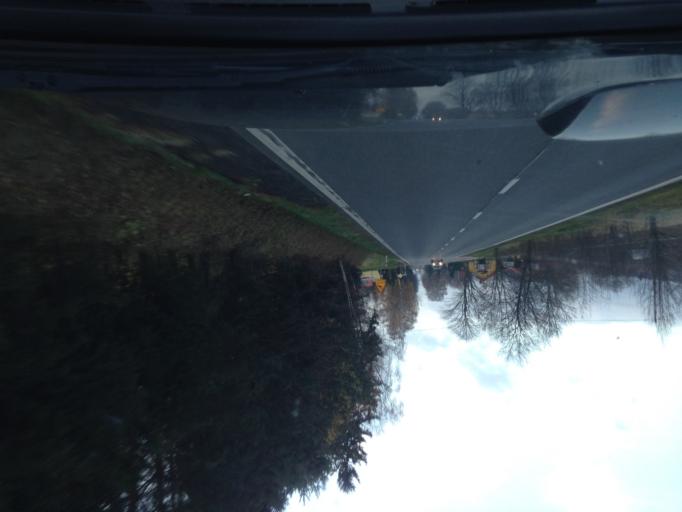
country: PL
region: Subcarpathian Voivodeship
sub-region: Powiat jasielski
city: Osiek Jasielski
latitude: 49.6434
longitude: 21.5164
